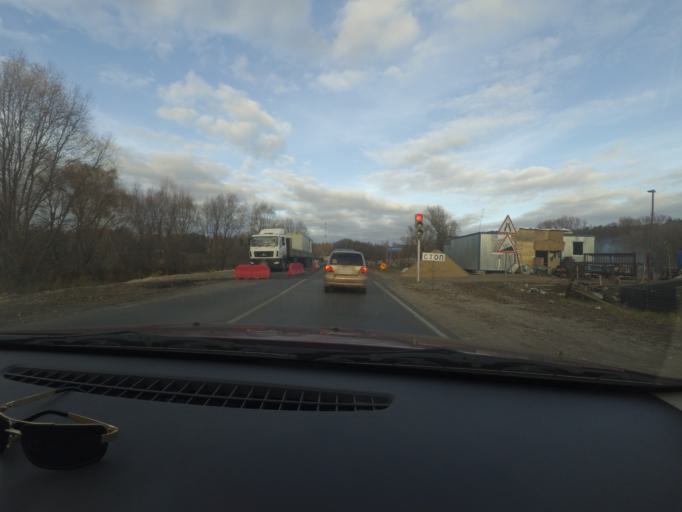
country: RU
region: Vladimir
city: Murom
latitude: 55.5229
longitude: 41.9504
